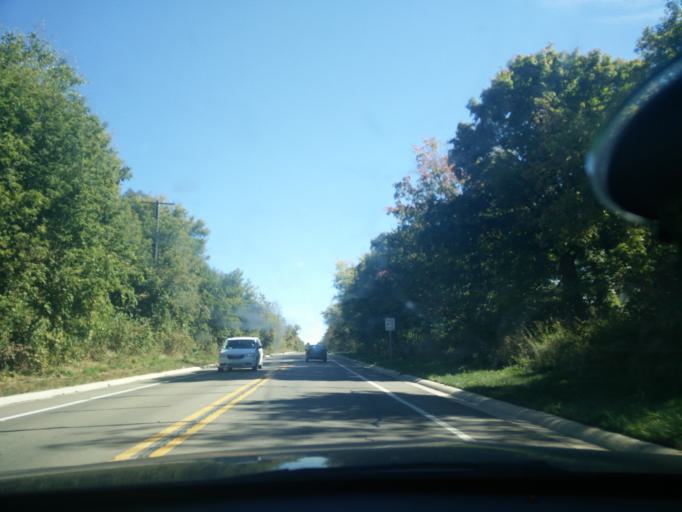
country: US
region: Michigan
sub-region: Wayne County
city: Northville
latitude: 42.4353
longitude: -83.5471
